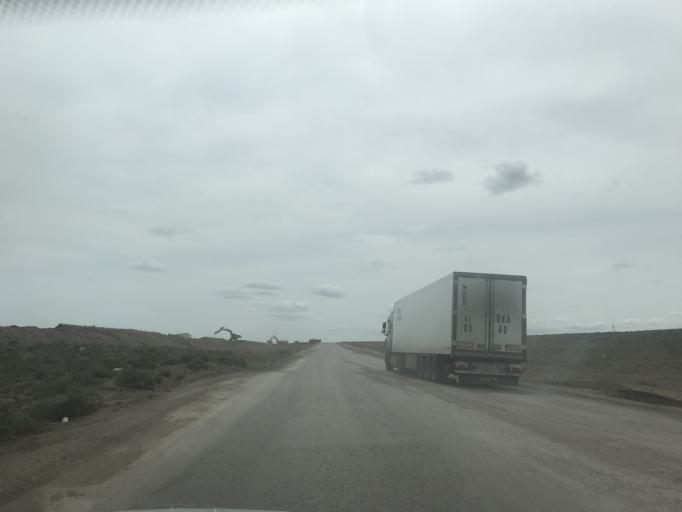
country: KZ
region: Zhambyl
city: Mynaral
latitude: 45.2661
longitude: 73.7938
